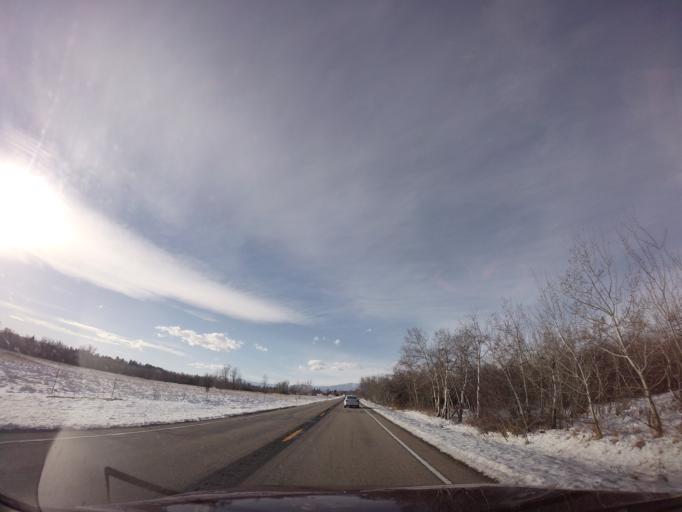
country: US
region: Montana
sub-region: Carbon County
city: Red Lodge
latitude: 45.3683
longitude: -109.1603
